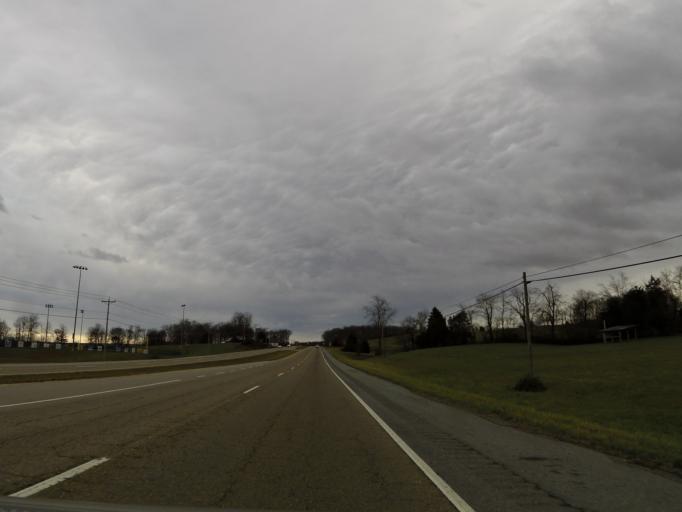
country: US
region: Tennessee
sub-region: Washington County
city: Jonesborough
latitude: 36.2593
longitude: -82.5663
